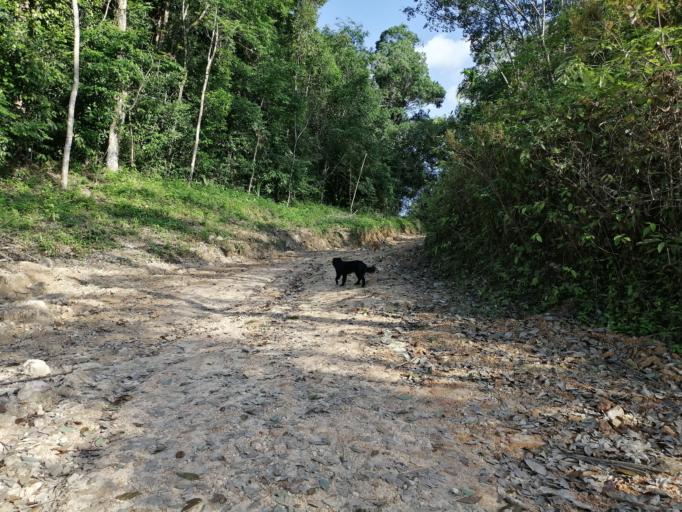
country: TH
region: Phatthalung
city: Pa Phayom
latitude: 7.9387
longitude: 99.8054
